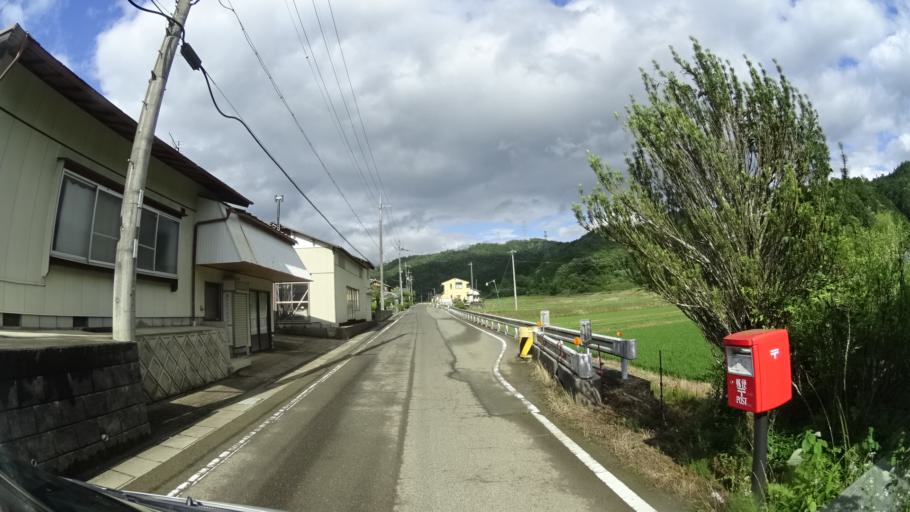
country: JP
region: Kyoto
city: Ayabe
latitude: 35.3670
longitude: 135.2662
